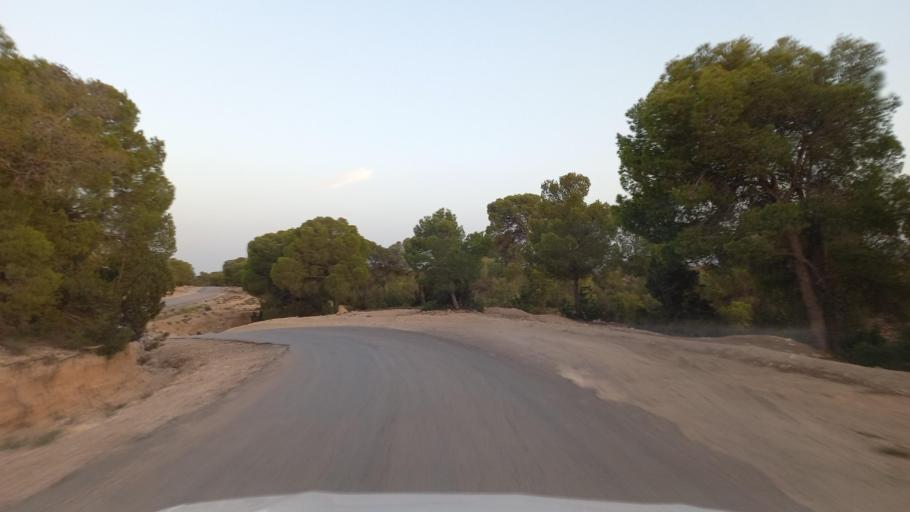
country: TN
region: Al Qasrayn
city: Sbiba
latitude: 35.4109
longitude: 8.9449
